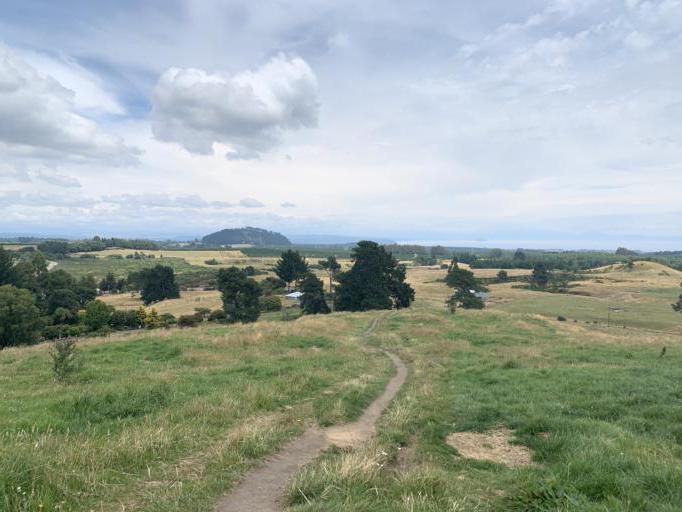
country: NZ
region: Waikato
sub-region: Taupo District
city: Taupo
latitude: -38.7025
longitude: 176.1419
